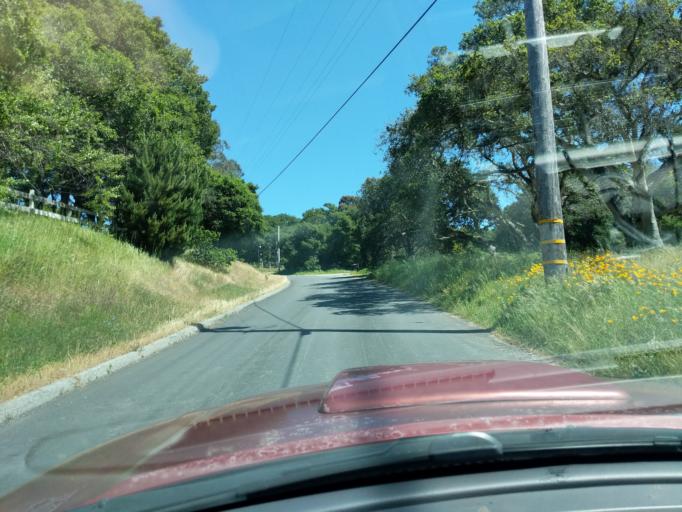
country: US
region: California
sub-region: Monterey County
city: Las Lomas
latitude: 36.8704
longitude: -121.6890
